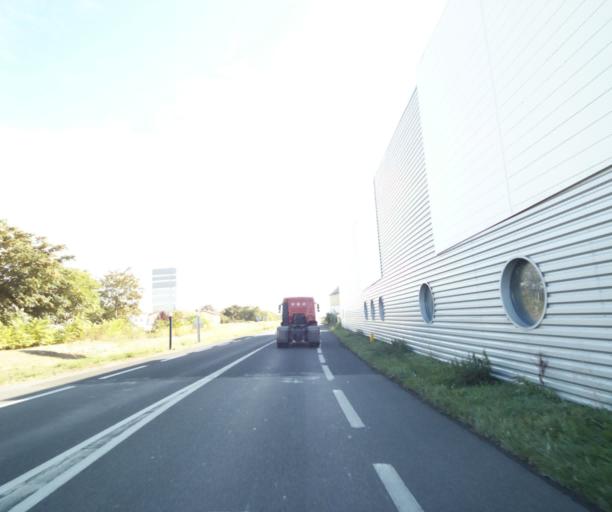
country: FR
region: Auvergne
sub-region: Departement du Puy-de-Dome
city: Aulnat
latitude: 45.7917
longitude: 3.1666
